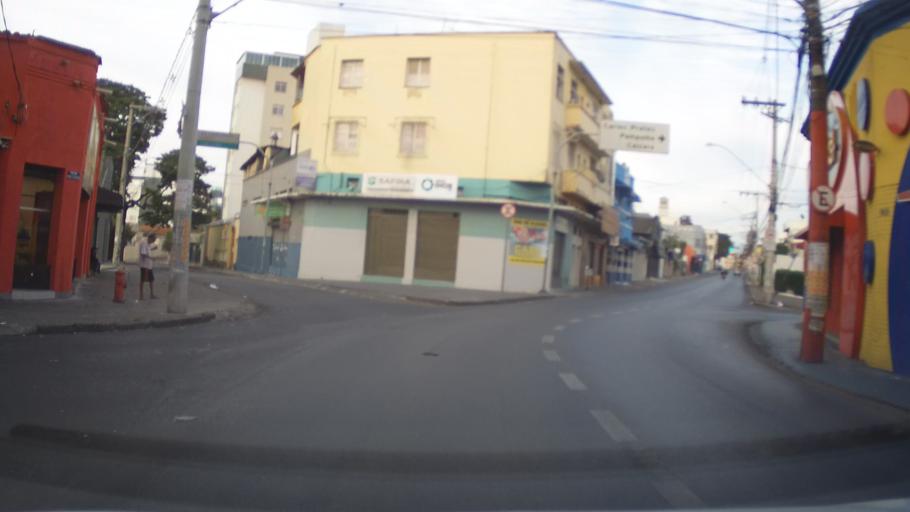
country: BR
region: Minas Gerais
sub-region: Belo Horizonte
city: Belo Horizonte
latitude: -19.9152
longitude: -43.9714
